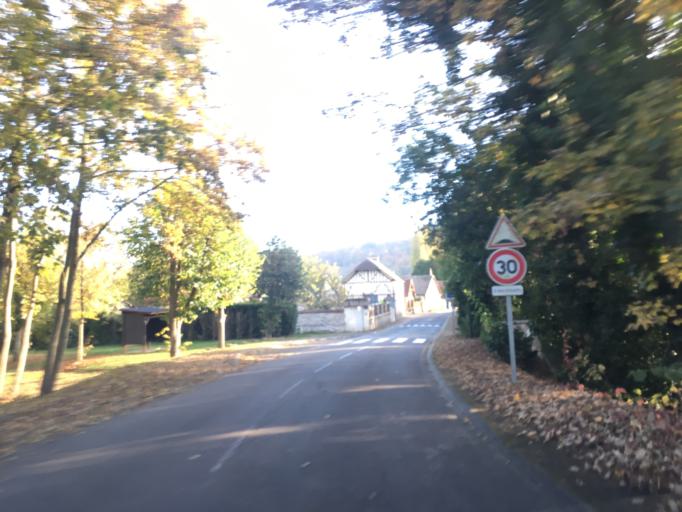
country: FR
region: Haute-Normandie
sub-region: Departement de l'Eure
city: Heudreville-sur-Eure
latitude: 49.1030
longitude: 1.2412
